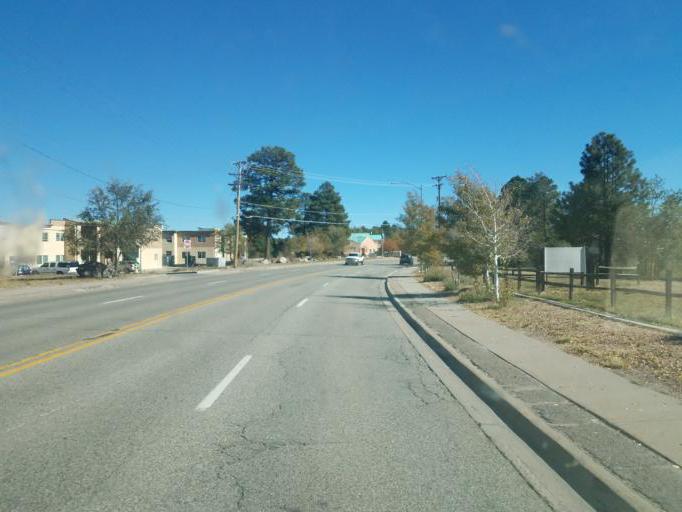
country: US
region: New Mexico
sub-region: Los Alamos County
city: Los Alamos
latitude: 35.8830
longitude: -106.3133
